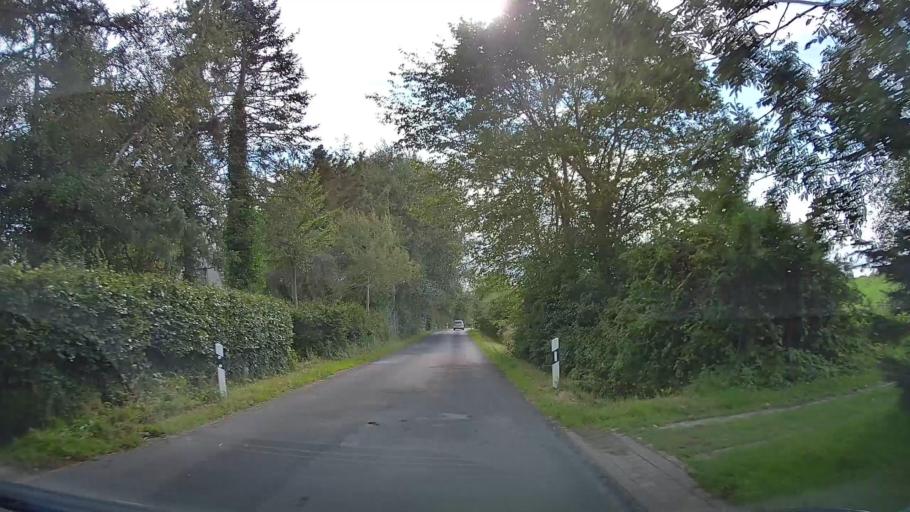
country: DE
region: Schleswig-Holstein
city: Ringsberg
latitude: 54.8332
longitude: 9.5887
